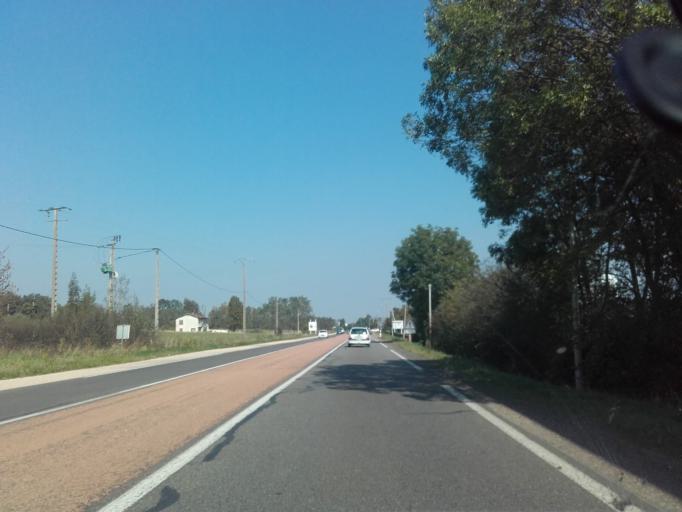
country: FR
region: Bourgogne
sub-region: Departement de Saone-et-Loire
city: Creches-sur-Saone
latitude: 46.2221
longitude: 4.7818
